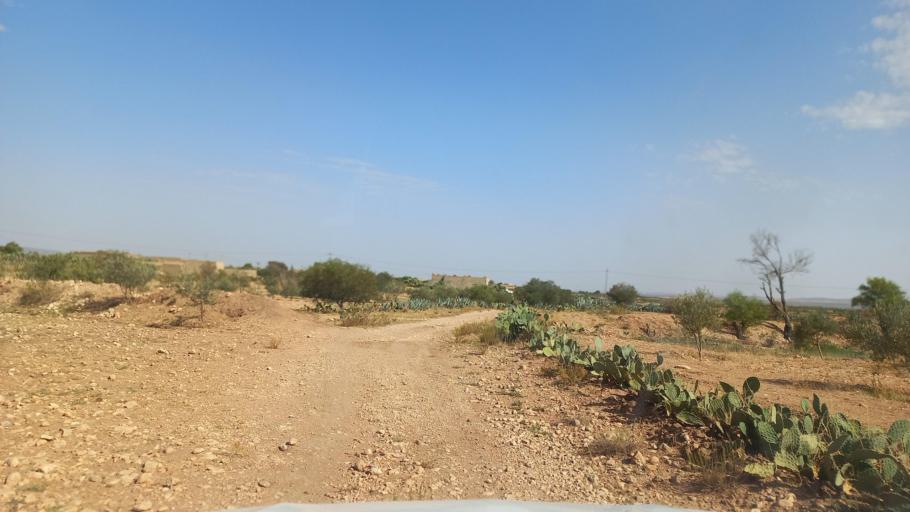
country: TN
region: Al Qasrayn
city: Kasserine
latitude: 35.2803
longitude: 8.9550
